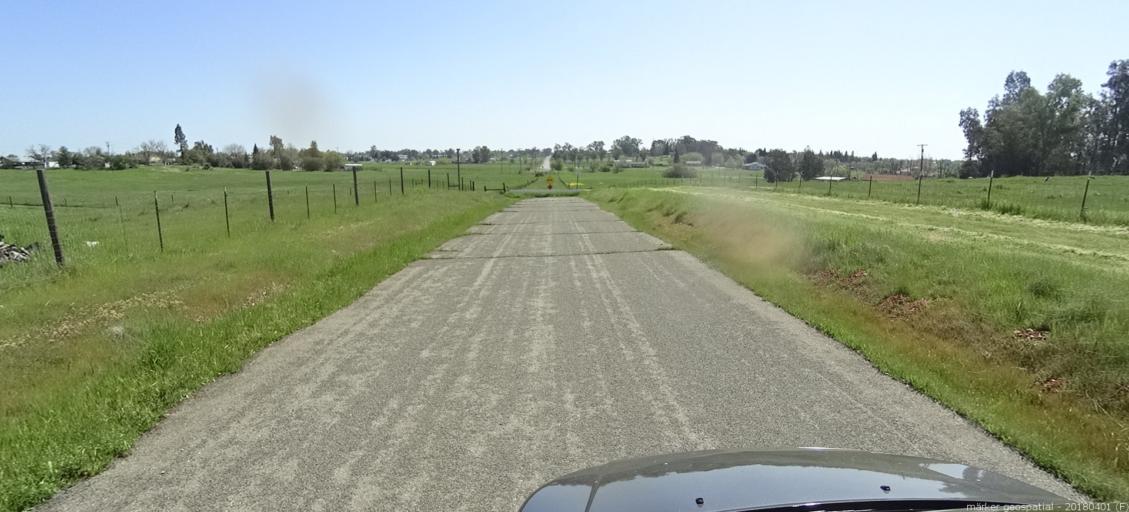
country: US
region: California
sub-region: Sacramento County
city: Wilton
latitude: 38.4020
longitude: -121.2424
